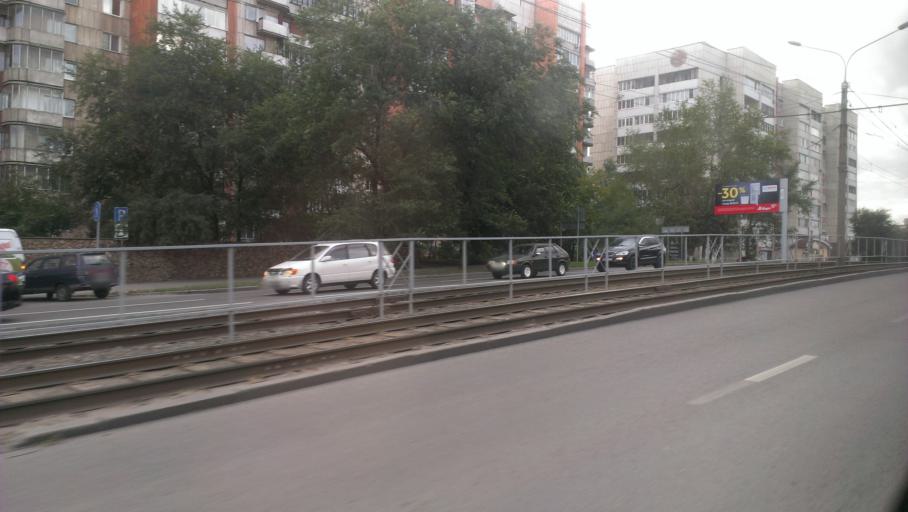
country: RU
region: Altai Krai
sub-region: Gorod Barnaulskiy
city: Barnaul
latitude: 53.3434
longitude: 83.7683
